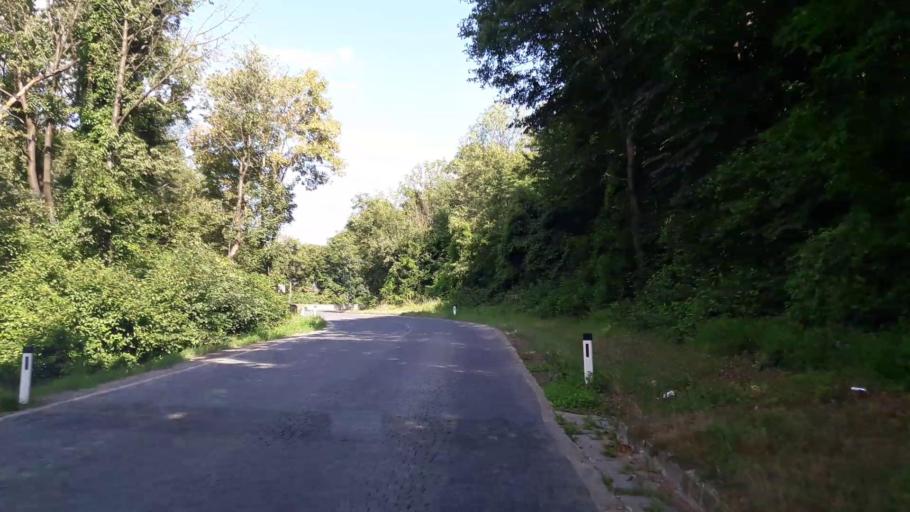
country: AT
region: Lower Austria
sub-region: Politischer Bezirk Wien-Umgebung
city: Klosterneuburg
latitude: 48.2852
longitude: 16.3249
